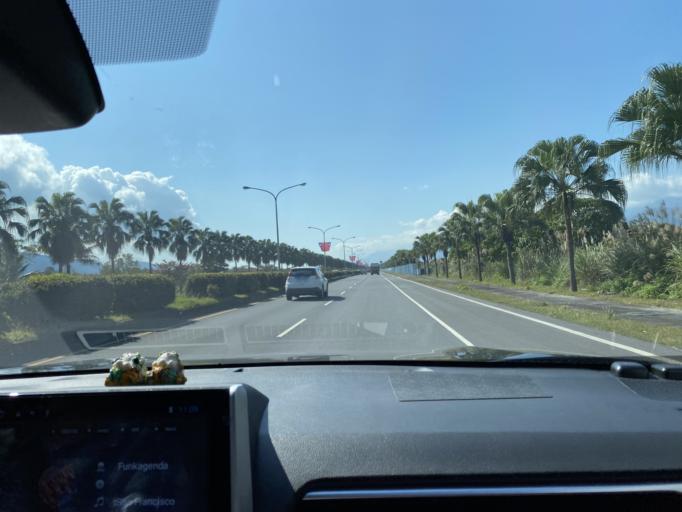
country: TW
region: Taiwan
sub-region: Hualien
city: Hualian
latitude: 23.8724
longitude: 121.5367
